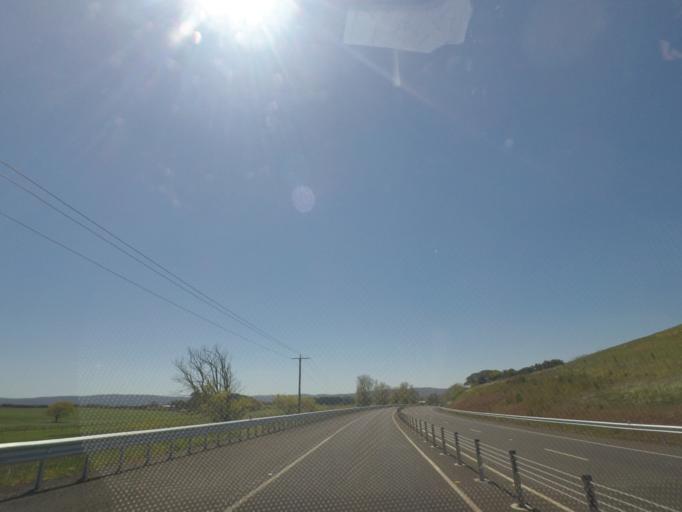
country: AU
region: Victoria
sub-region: Hume
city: Sunbury
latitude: -37.2971
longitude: 144.7365
